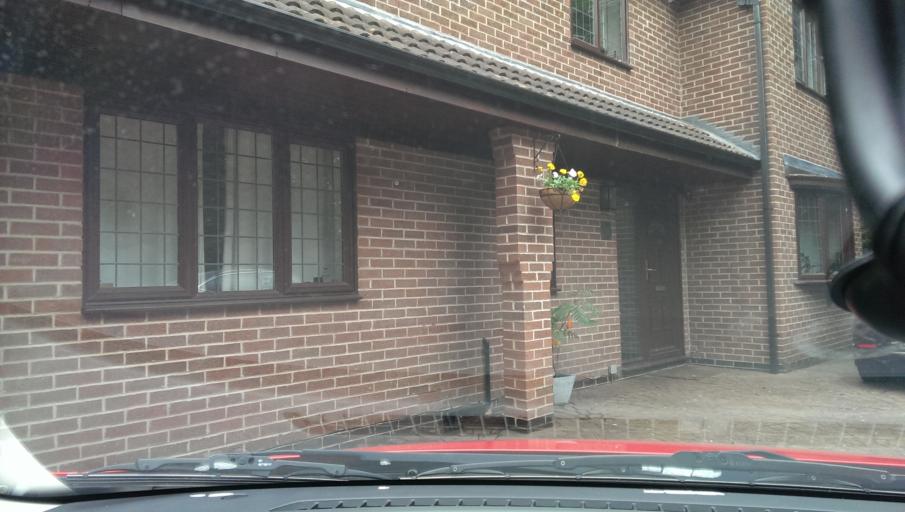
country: GB
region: England
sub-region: Leicestershire
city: Narborough
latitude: 52.5679
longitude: -1.1991
